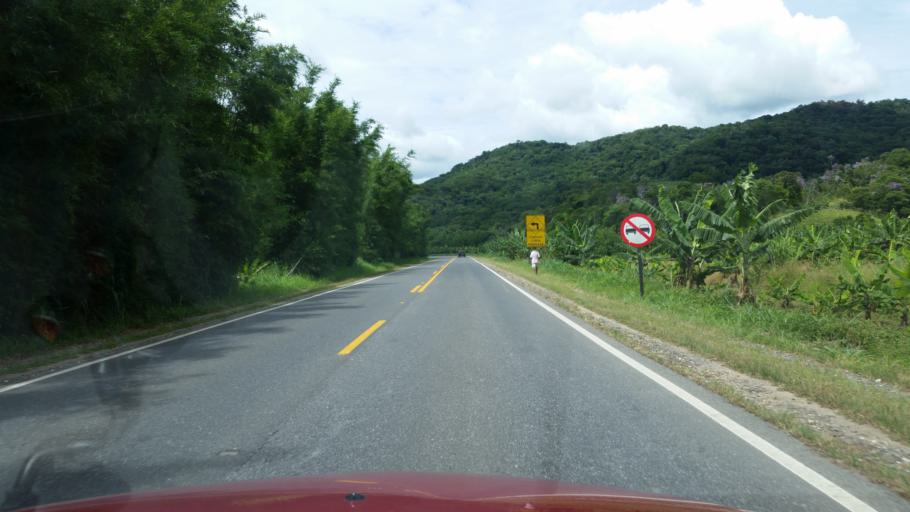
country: BR
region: Sao Paulo
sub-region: Miracatu
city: Miracatu
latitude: -24.3870
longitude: -47.5277
